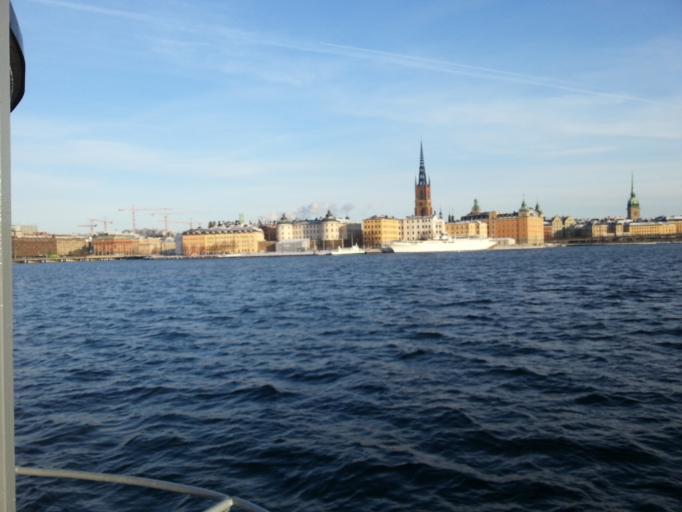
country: SE
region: Stockholm
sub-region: Stockholms Kommun
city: Stockholm
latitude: 59.3223
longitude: 18.0571
